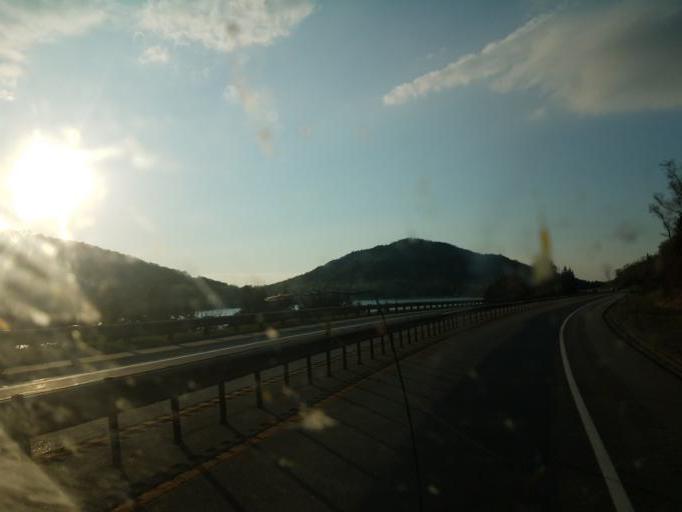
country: US
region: New Hampshire
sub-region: Grafton County
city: Deerfield
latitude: 44.1725
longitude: -71.6884
